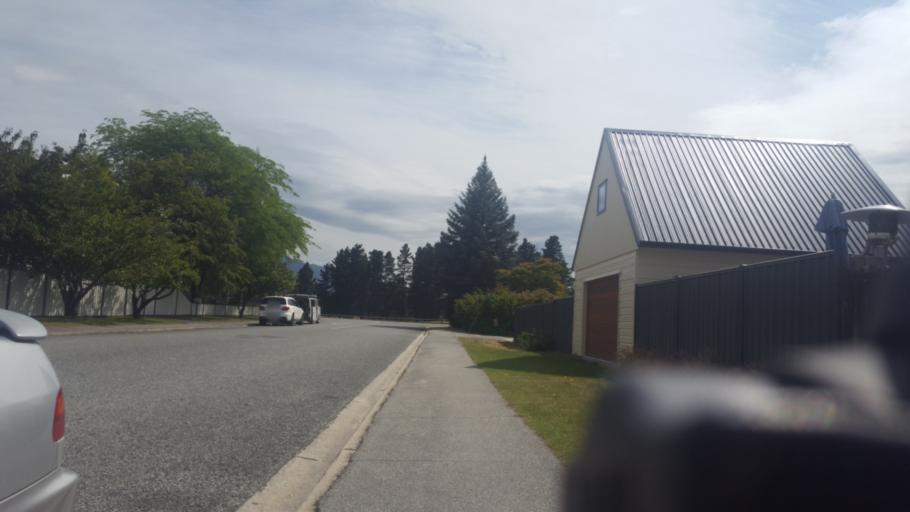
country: NZ
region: Otago
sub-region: Queenstown-Lakes District
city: Wanaka
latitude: -45.0408
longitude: 169.2020
